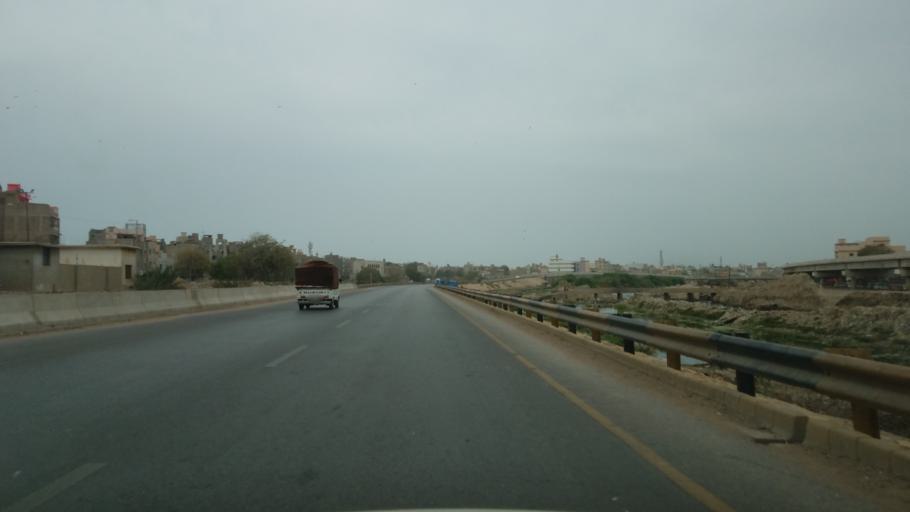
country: PK
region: Sindh
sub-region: Karachi District
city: Karachi
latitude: 24.8803
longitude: 67.0178
